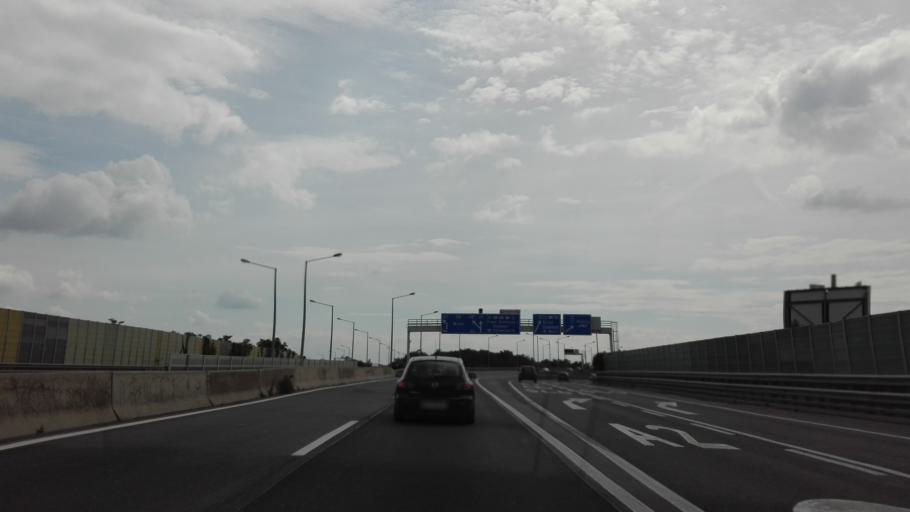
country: AT
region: Lower Austria
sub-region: Politischer Bezirk Modling
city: Vosendorf
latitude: 48.1212
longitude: 16.3169
